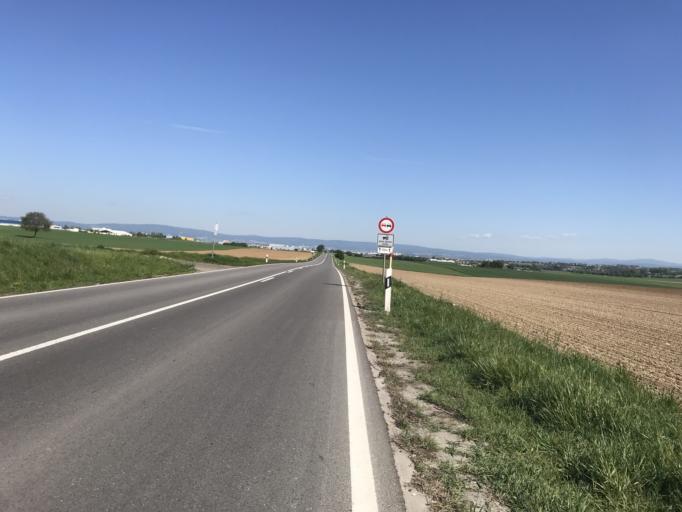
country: DE
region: Rheinland-Pfalz
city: Gau-Bischofsheim
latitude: 49.9291
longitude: 8.2666
